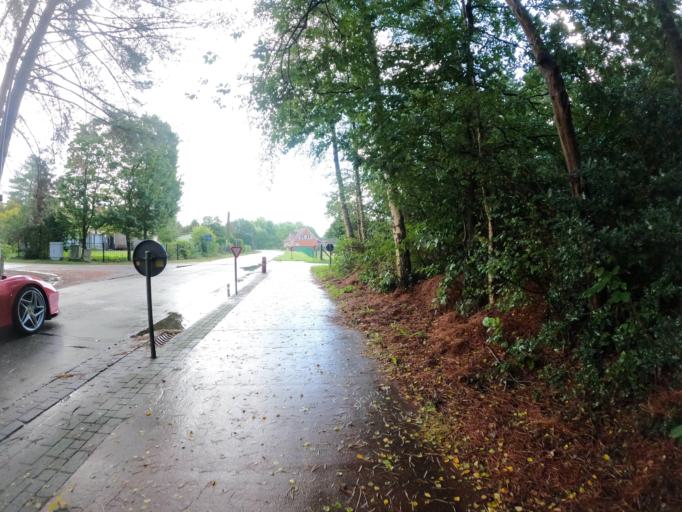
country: BE
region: Flanders
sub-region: Provincie Antwerpen
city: Lille
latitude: 51.2271
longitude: 4.8185
